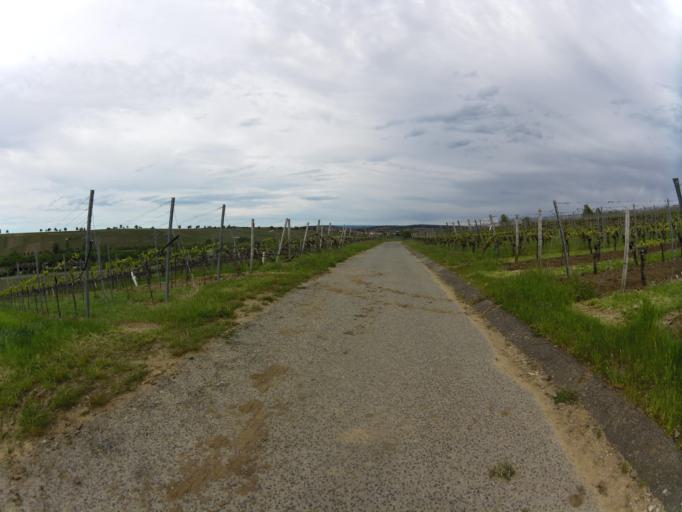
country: DE
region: Bavaria
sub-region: Regierungsbezirk Unterfranken
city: Nordheim
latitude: 49.8571
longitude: 10.1936
